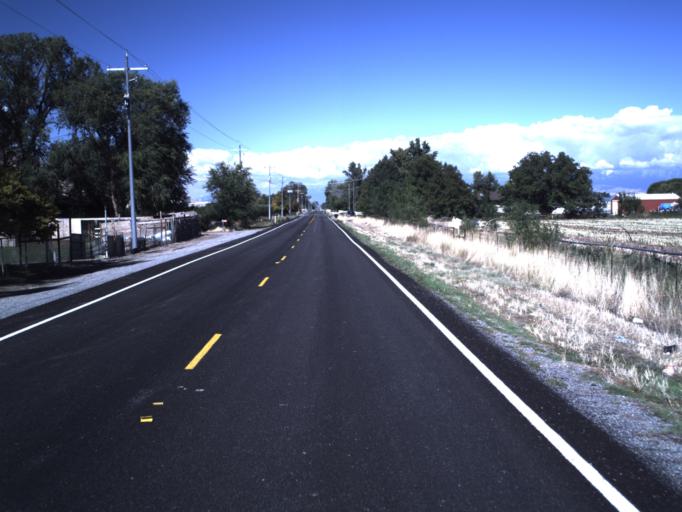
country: US
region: Utah
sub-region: Utah County
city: West Mountain
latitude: 40.0292
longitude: -111.7871
